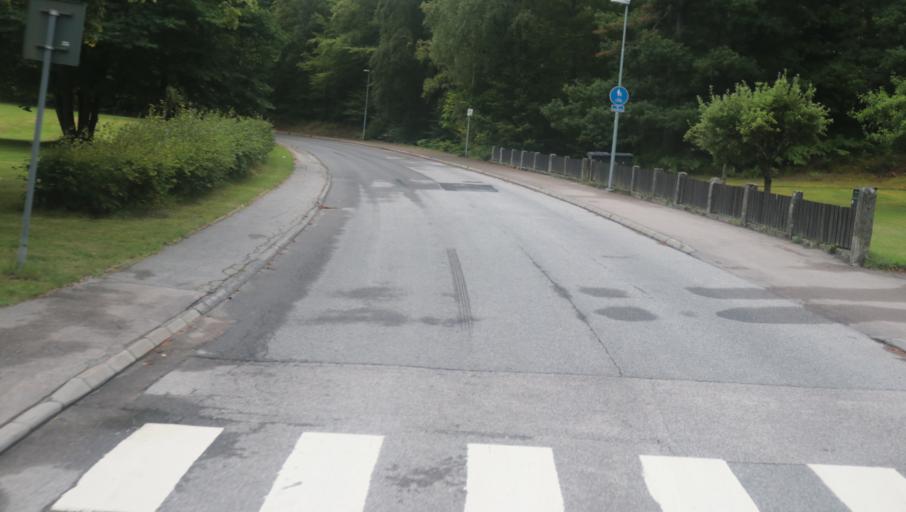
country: SE
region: Blekinge
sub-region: Karlshamns Kommun
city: Svangsta
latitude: 56.2612
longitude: 14.7736
